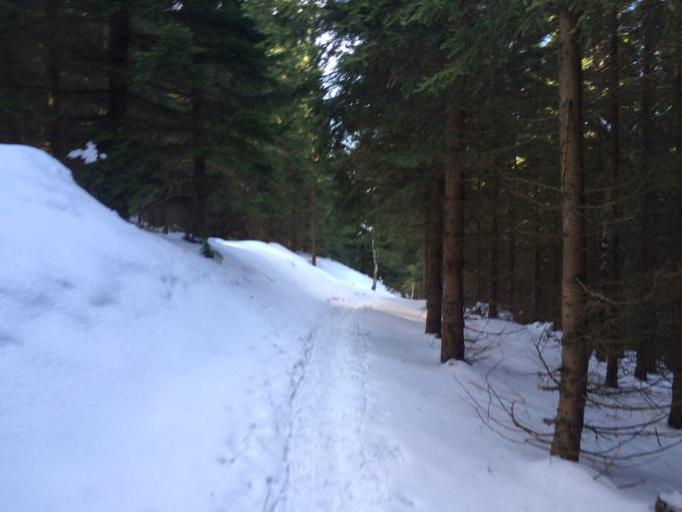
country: CZ
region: Olomoucky
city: Vapenna
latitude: 50.2605
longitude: 17.0075
